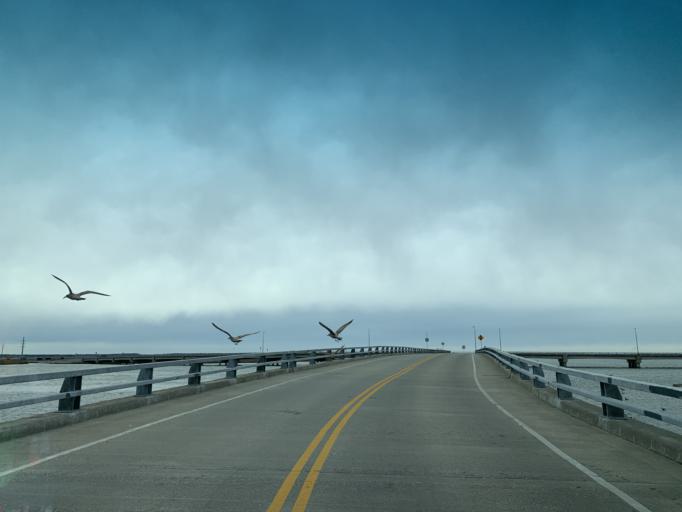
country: US
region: Virginia
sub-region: Accomack County
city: Chincoteague
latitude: 37.9360
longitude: -75.3805
